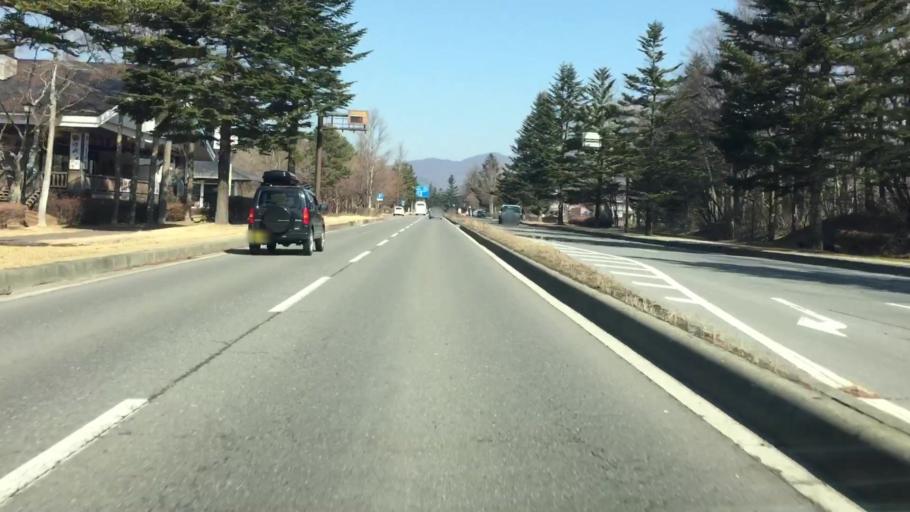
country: JP
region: Nagano
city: Saku
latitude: 36.3362
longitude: 138.6311
